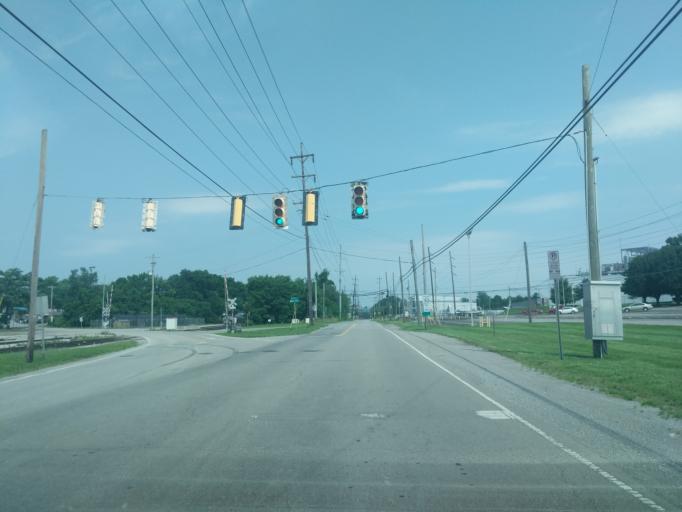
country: US
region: Tennessee
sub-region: Davidson County
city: Lakewood
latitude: 36.2699
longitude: -86.6604
